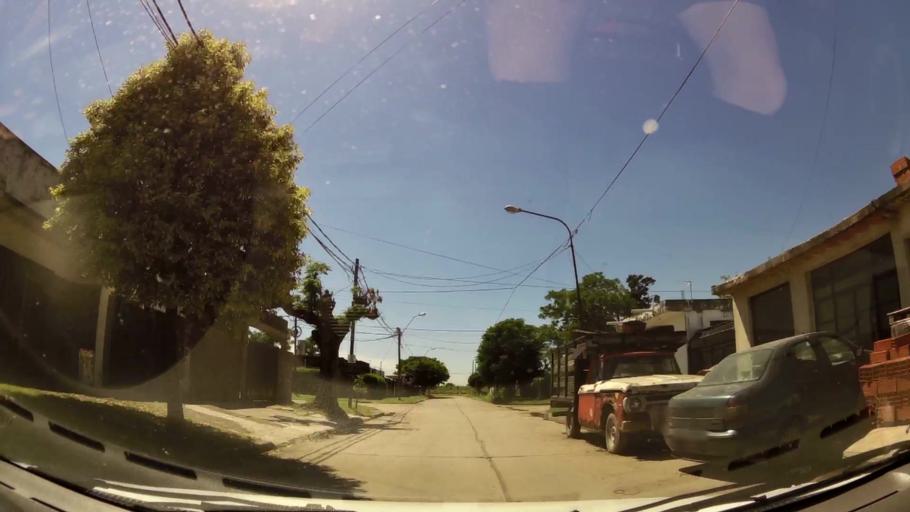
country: AR
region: Buenos Aires
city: Ituzaingo
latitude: -34.6798
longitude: -58.6574
